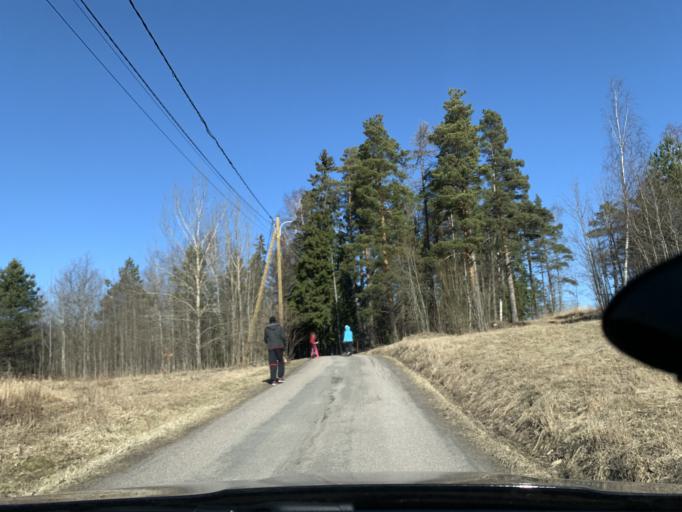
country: FI
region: Uusimaa
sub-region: Helsinki
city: Espoo
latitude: 60.1720
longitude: 24.5827
